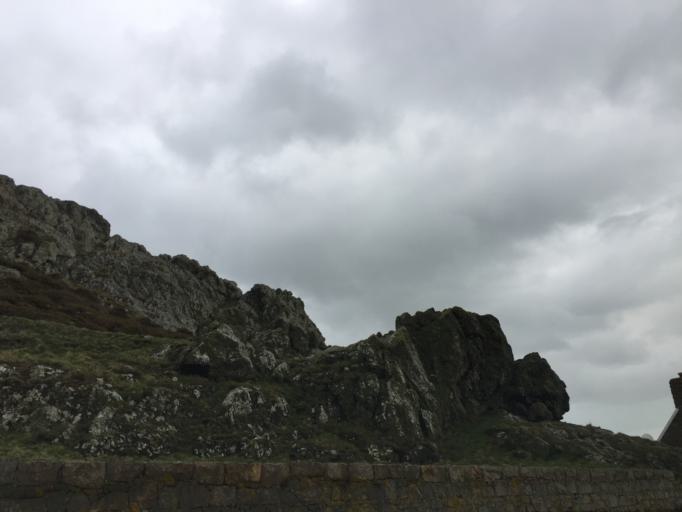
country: JE
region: St Helier
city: Saint Helier
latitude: 49.2415
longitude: -2.2498
